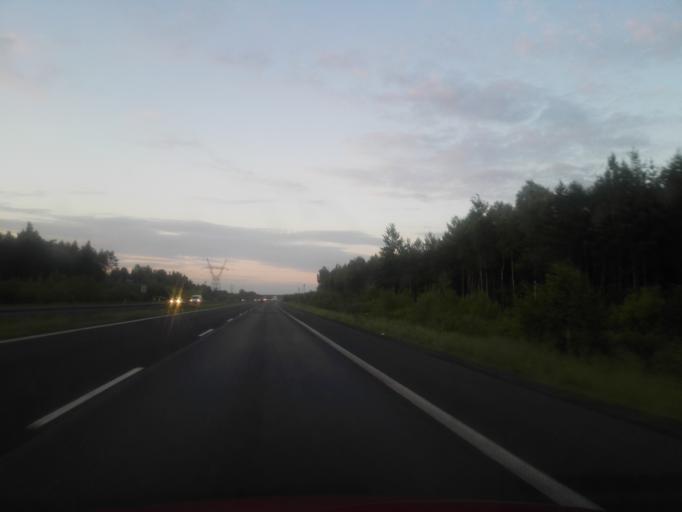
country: PL
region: Silesian Voivodeship
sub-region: Powiat czestochowski
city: Borowno
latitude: 51.0187
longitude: 19.3141
